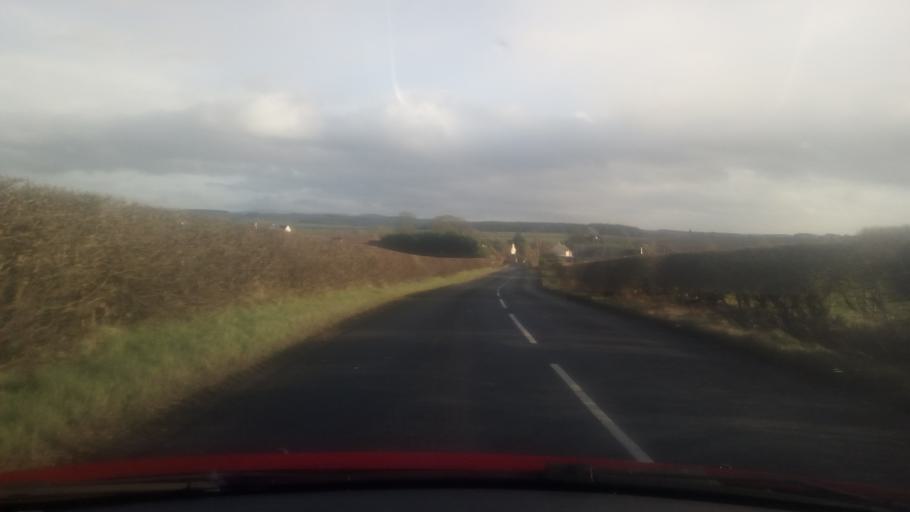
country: GB
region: Scotland
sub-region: The Scottish Borders
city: Kelso
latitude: 55.6312
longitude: -2.4191
